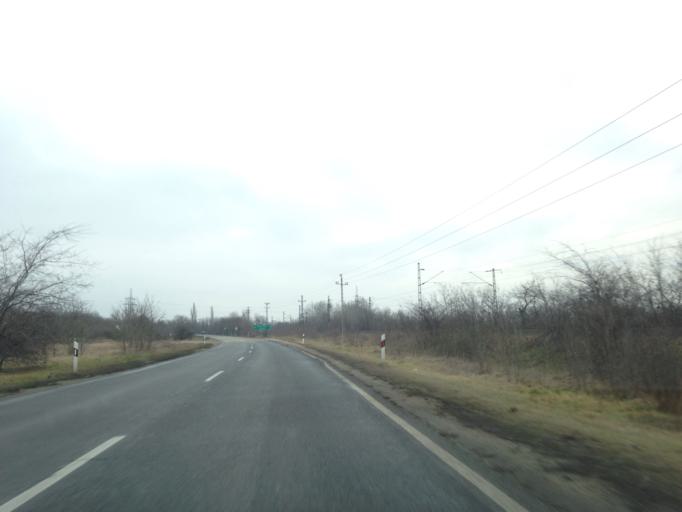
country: HU
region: Komarom-Esztergom
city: Szomod
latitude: 47.6794
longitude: 18.3172
